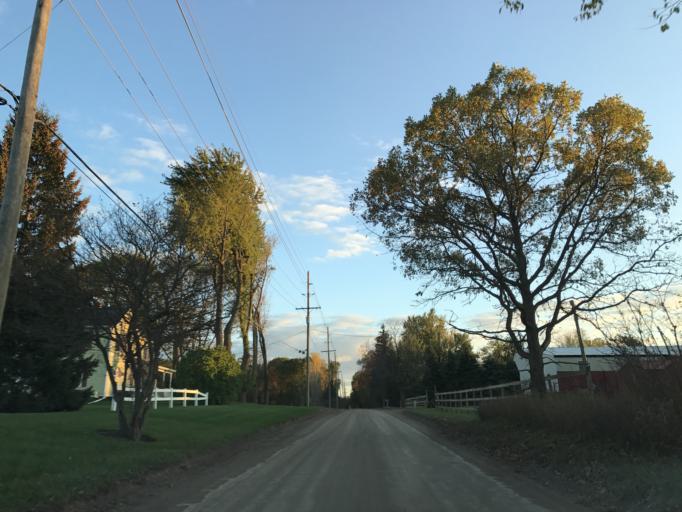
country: US
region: Michigan
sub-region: Oakland County
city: South Lyon
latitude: 42.4928
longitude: -83.6387
